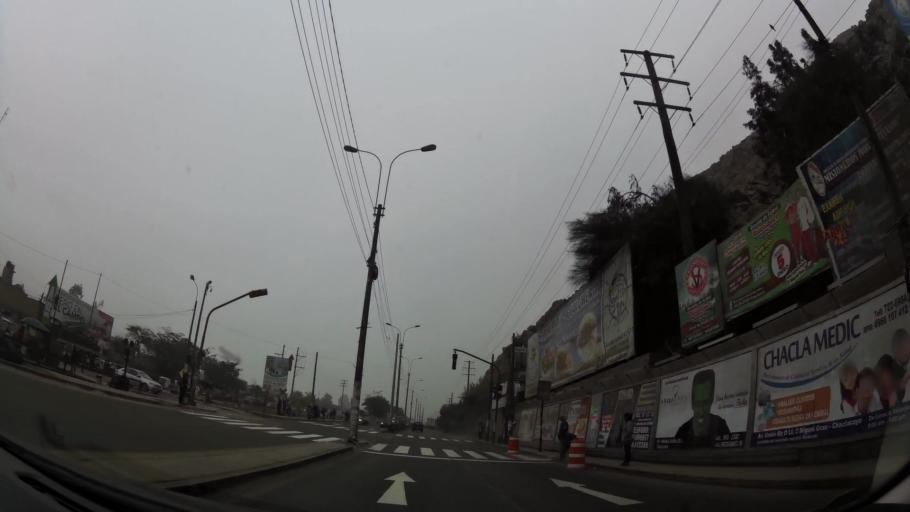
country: PE
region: Lima
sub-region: Lima
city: Chaclacayo
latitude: -11.9895
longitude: -76.8187
